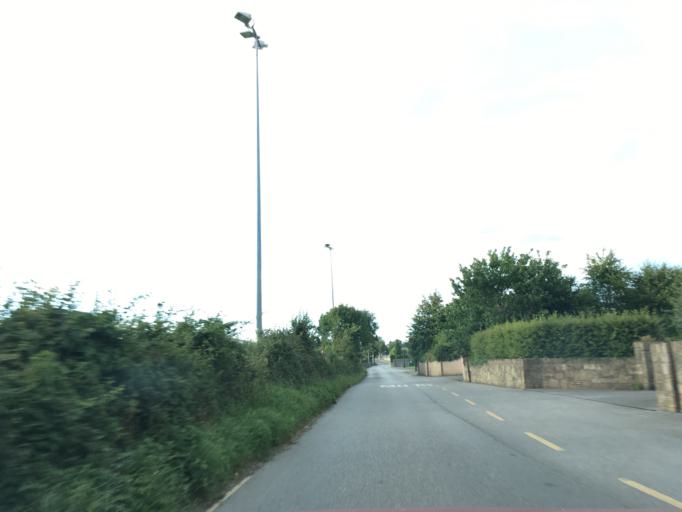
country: IE
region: Munster
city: Cashel
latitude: 52.5055
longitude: -7.8865
